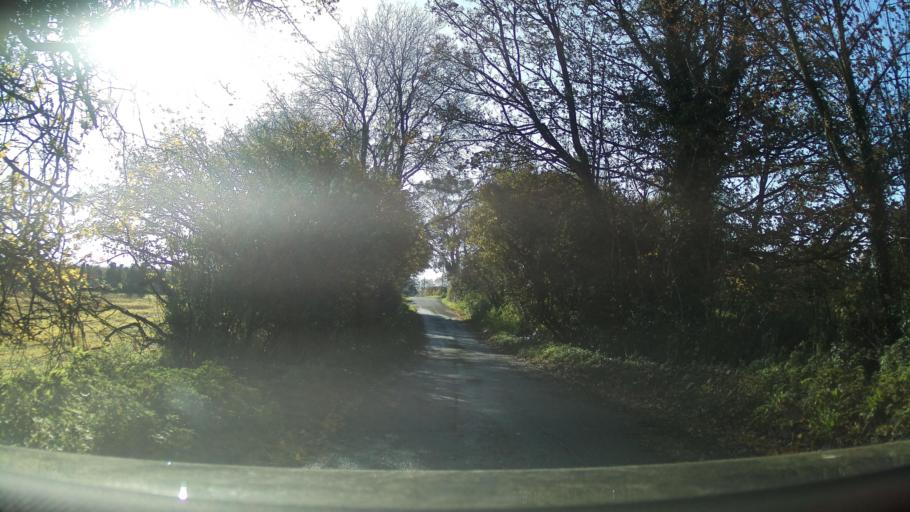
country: GB
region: England
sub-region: Somerset
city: Milborne Port
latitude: 51.0119
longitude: -2.5073
